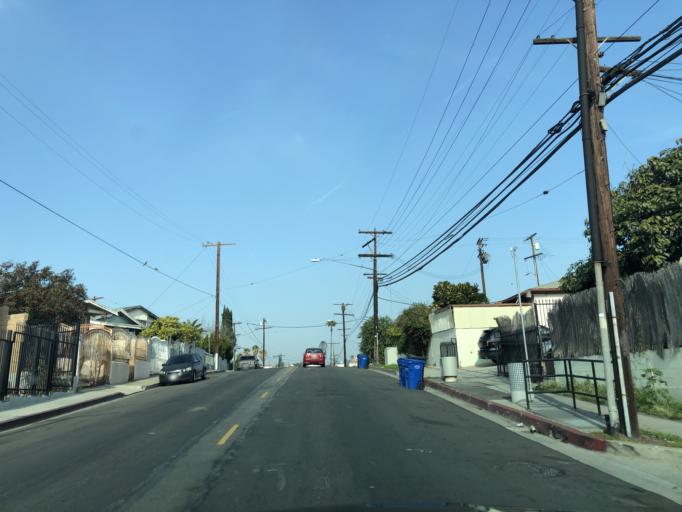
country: US
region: California
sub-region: Los Angeles County
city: Boyle Heights
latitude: 34.0375
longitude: -118.1924
